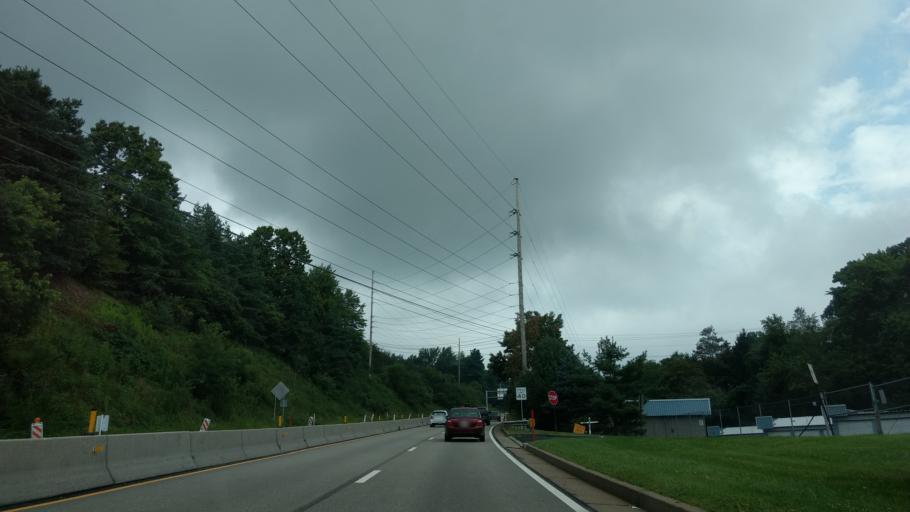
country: US
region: Pennsylvania
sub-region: Allegheny County
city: Franklin Park
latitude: 40.5924
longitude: -80.0477
